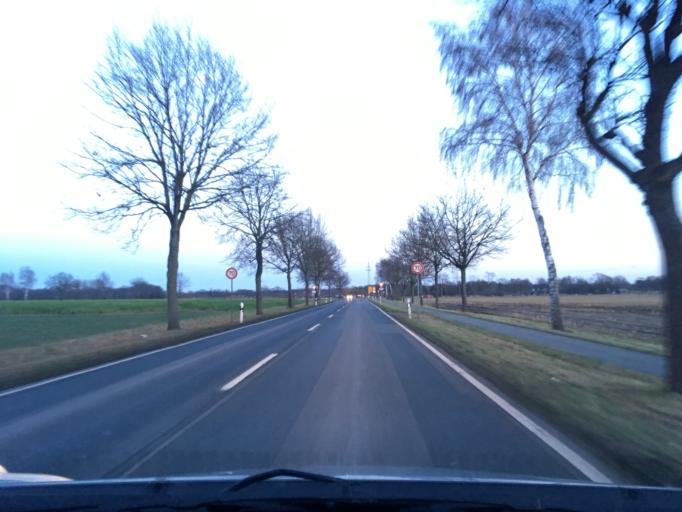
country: DE
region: Lower Saxony
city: Luechow
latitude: 52.9767
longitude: 11.1239
